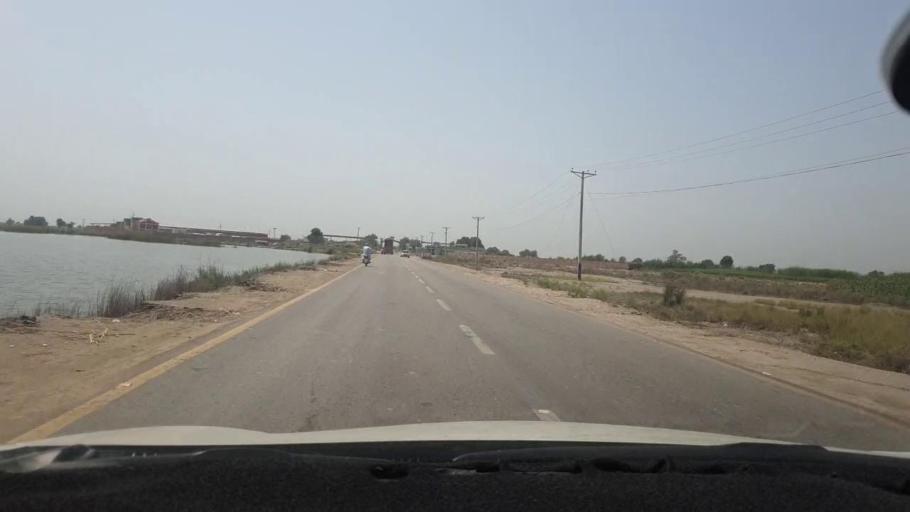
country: PK
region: Sindh
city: Shahdadpur
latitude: 25.9031
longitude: 68.5940
